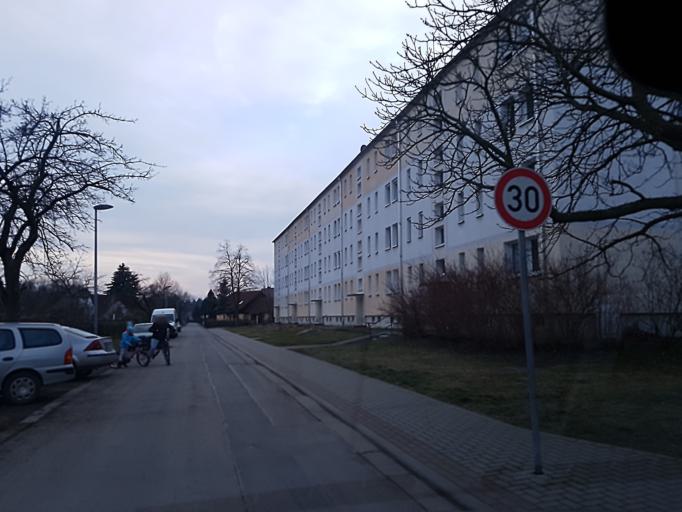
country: DE
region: Brandenburg
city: Doberlug-Kirchhain
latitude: 51.6345
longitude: 13.5666
